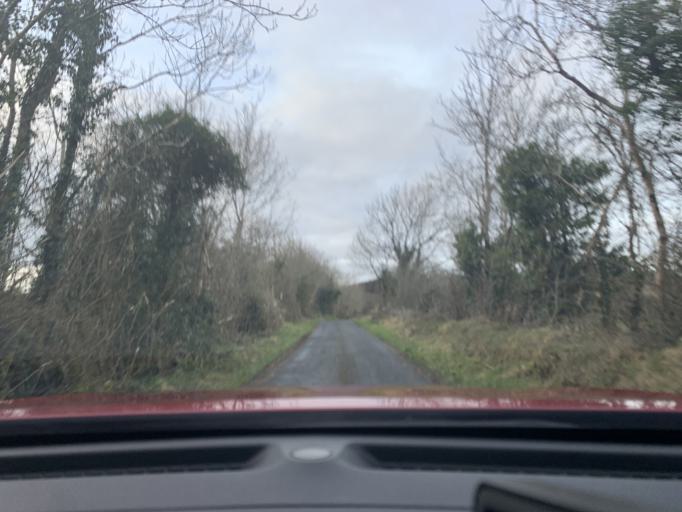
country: IE
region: Connaught
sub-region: Sligo
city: Ballymote
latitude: 54.0058
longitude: -8.5755
